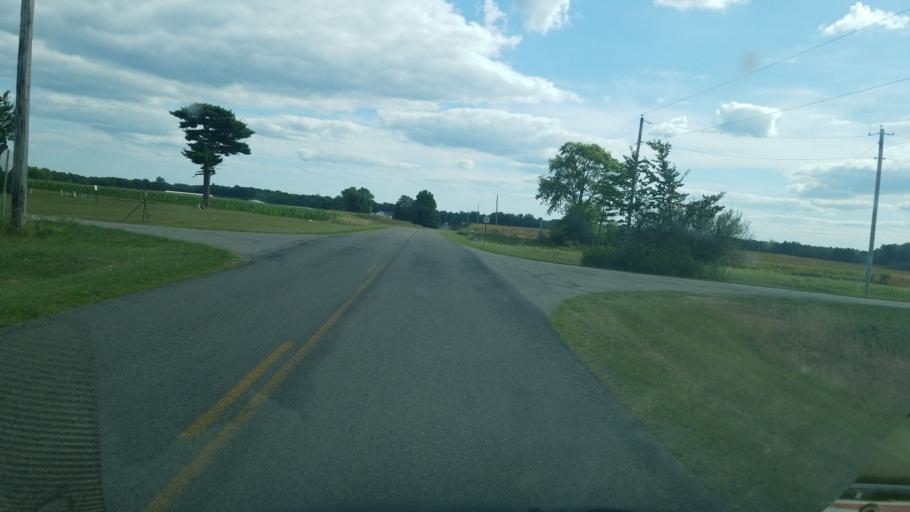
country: US
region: Ohio
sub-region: Logan County
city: De Graff
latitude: 40.2767
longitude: -83.9258
